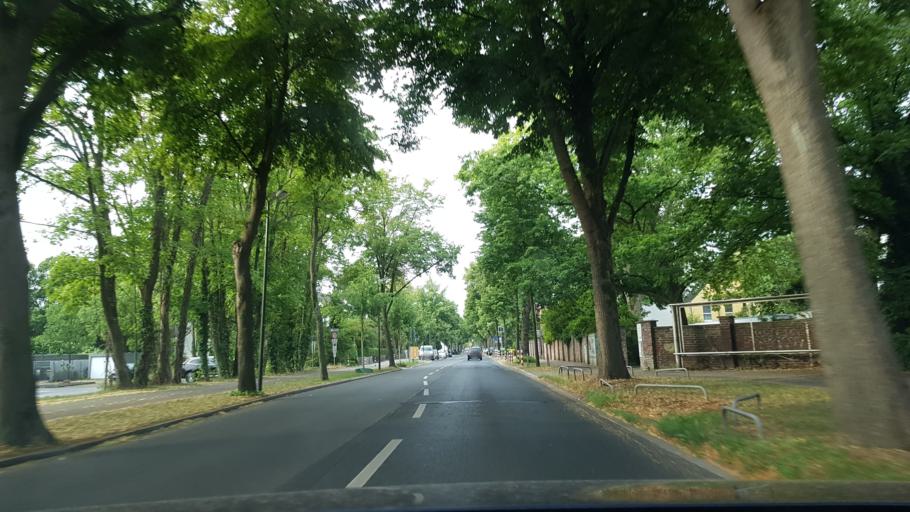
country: DE
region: North Rhine-Westphalia
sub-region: Regierungsbezirk Dusseldorf
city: Meerbusch
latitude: 51.2909
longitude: 6.7369
